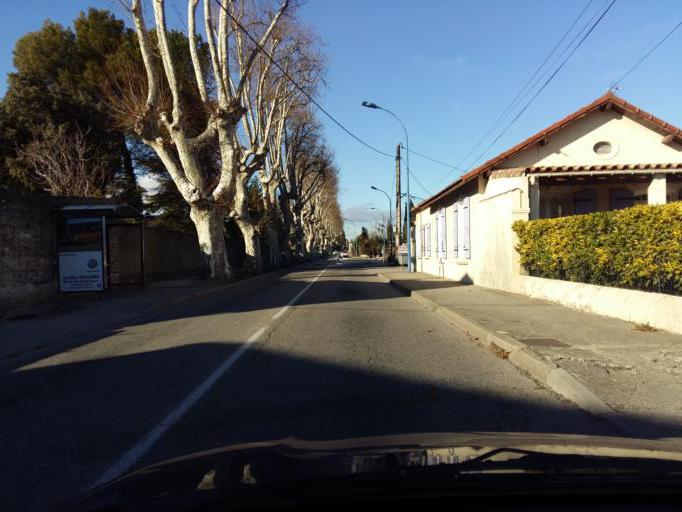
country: FR
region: Languedoc-Roussillon
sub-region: Departement du Gard
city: Pont-Saint-Esprit
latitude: 44.2636
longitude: 4.6414
